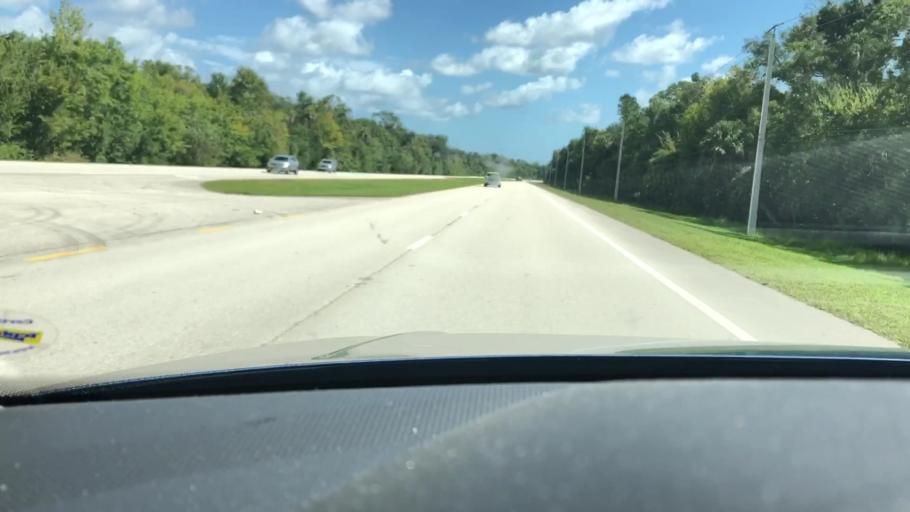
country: US
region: Florida
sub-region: Volusia County
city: Edgewater
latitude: 28.9582
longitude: -80.9297
